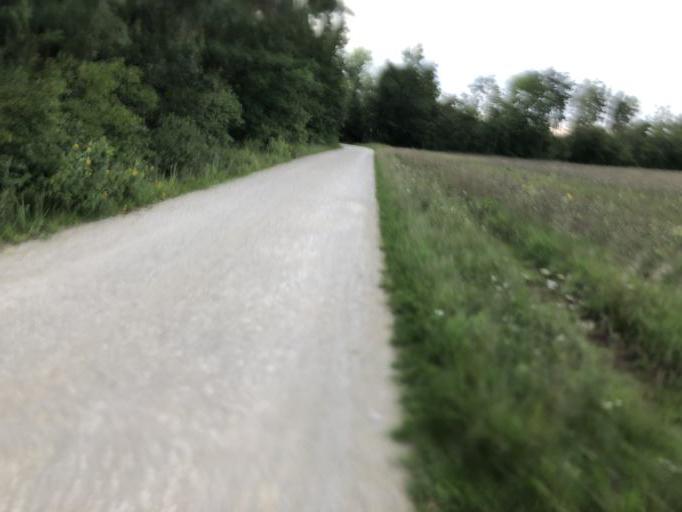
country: DE
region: Bavaria
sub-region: Regierungsbezirk Mittelfranken
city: Uttenreuth
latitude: 49.5884
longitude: 11.0756
